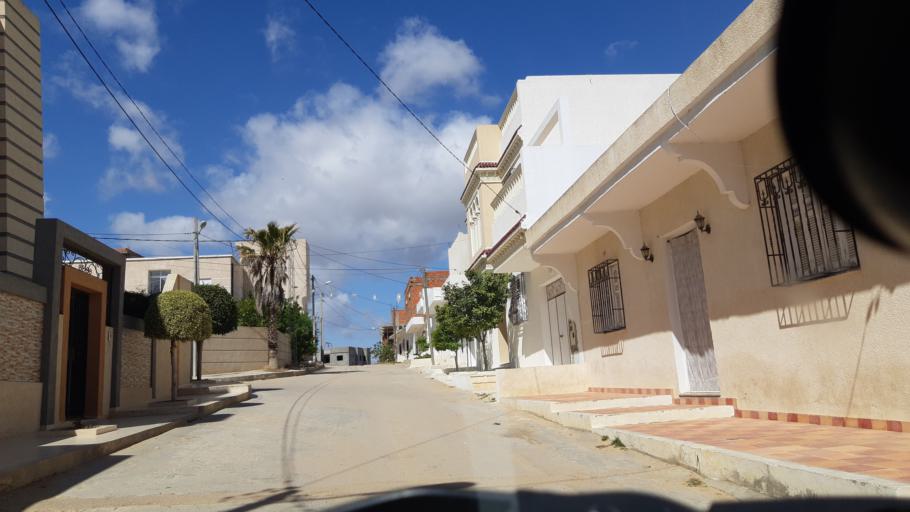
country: TN
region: Susah
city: Akouda
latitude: 35.8932
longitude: 10.5324
